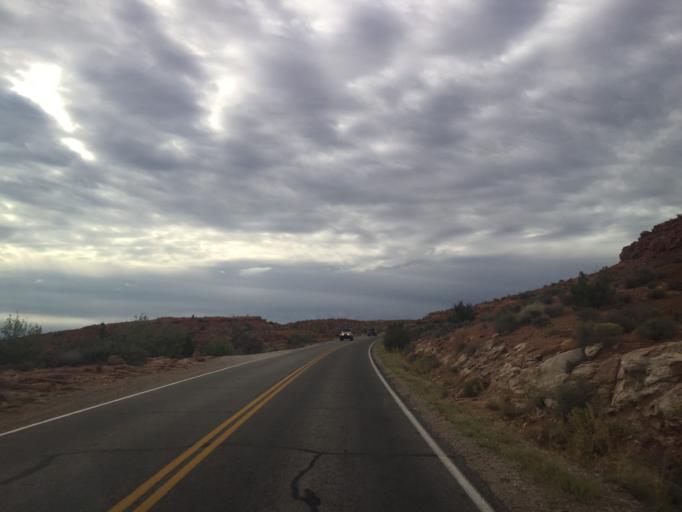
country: US
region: Utah
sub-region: Grand County
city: Moab
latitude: 38.6286
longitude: -109.5937
